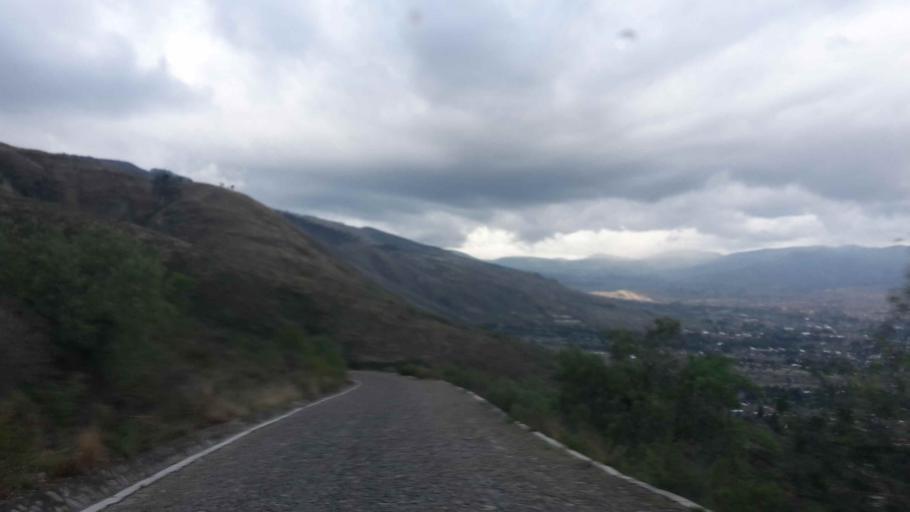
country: BO
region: Cochabamba
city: Cochabamba
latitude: -17.3686
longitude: -66.0637
